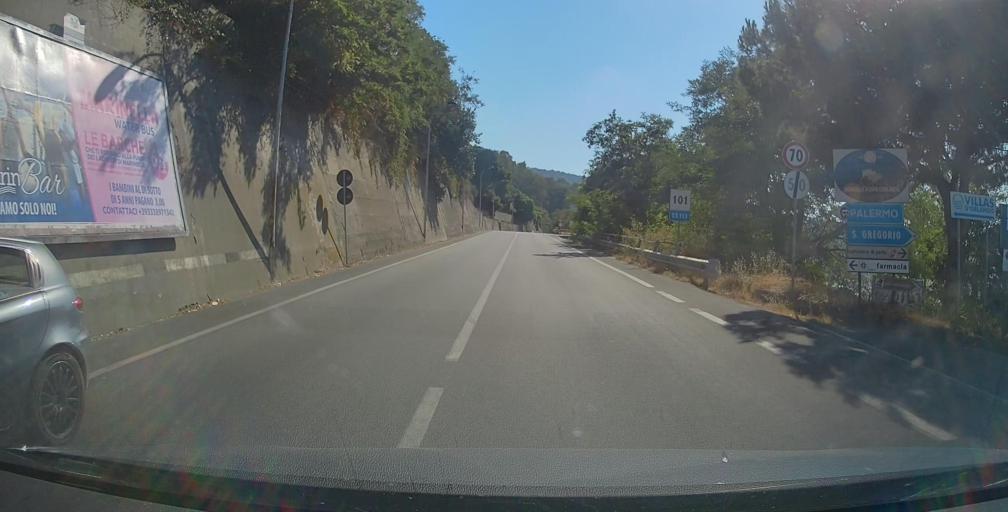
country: IT
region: Sicily
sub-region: Messina
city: Naso
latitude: 38.1539
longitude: 14.7778
